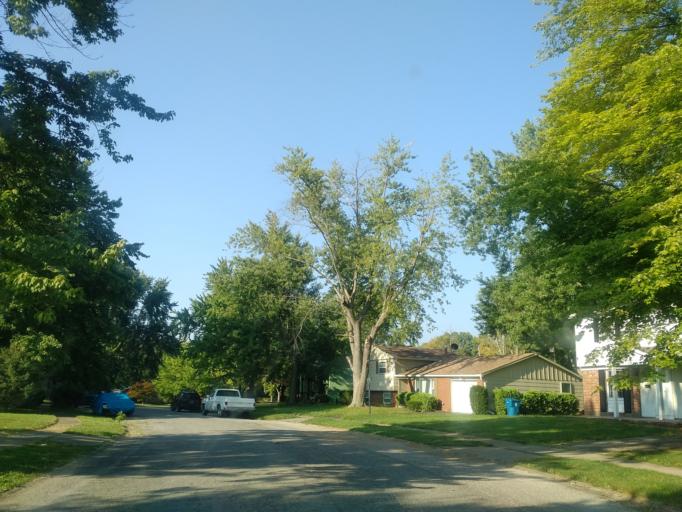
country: US
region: Indiana
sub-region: Marion County
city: Cumberland
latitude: 39.7932
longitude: -85.9880
